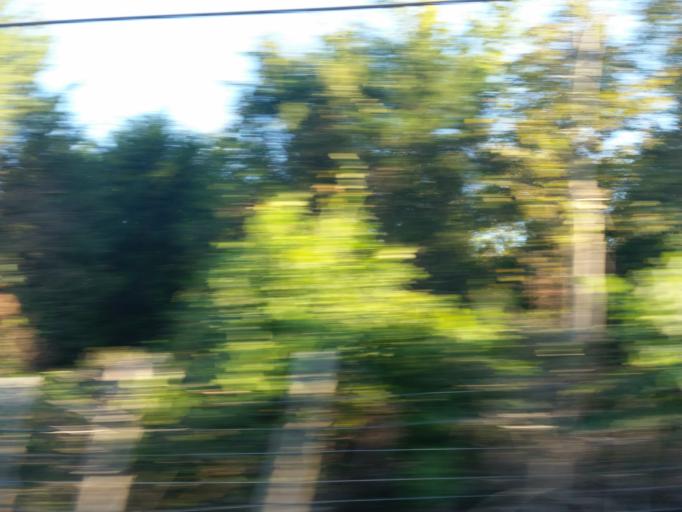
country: US
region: Tennessee
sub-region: Grainger County
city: Rutledge
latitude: 36.3484
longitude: -83.4529
